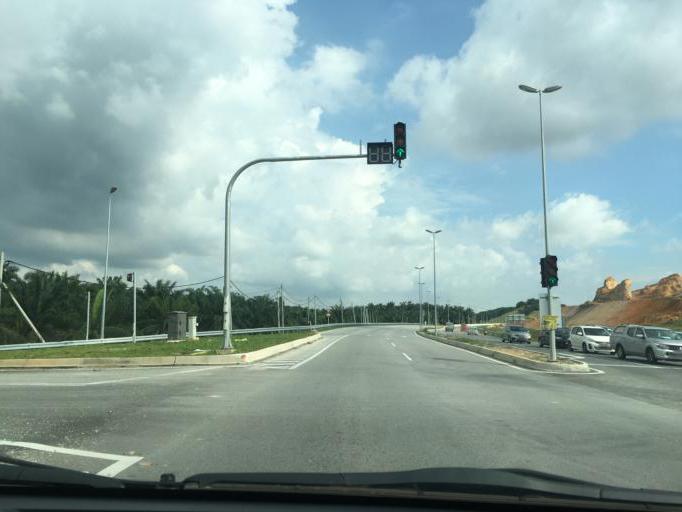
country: MY
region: Selangor
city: Batu Arang
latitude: 3.2964
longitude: 101.4403
